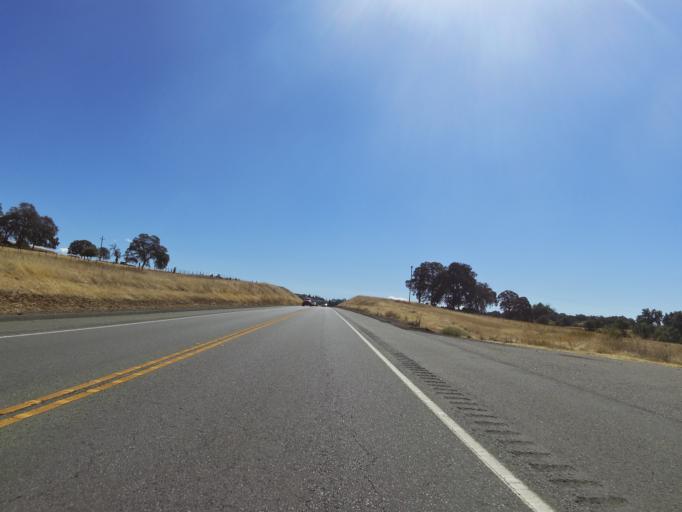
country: US
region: California
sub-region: Amador County
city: Sutter Creek
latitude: 38.3866
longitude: -120.8130
